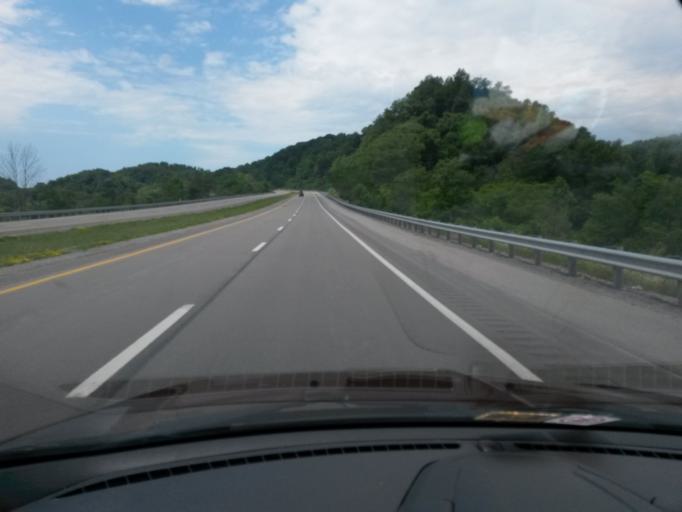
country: US
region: West Virginia
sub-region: Lewis County
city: Weston
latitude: 38.9034
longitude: -80.6114
